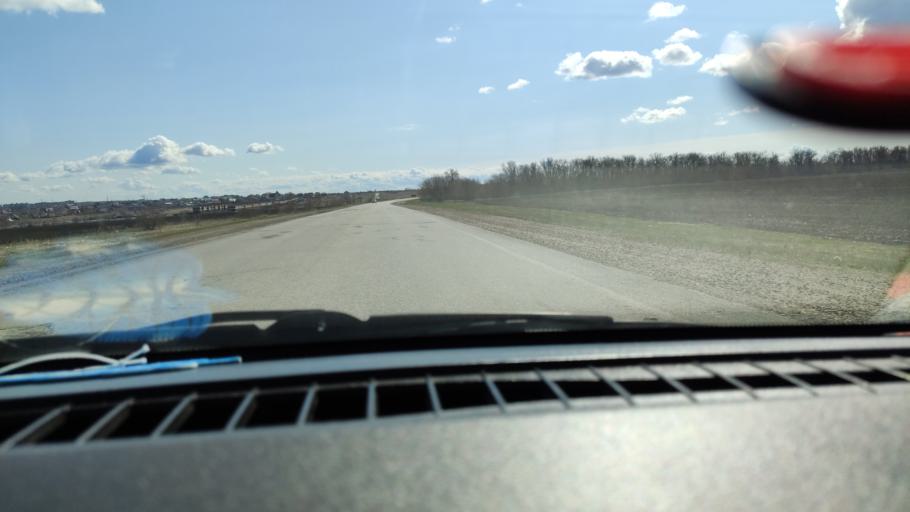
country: RU
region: Samara
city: Varlamovo
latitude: 53.1159
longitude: 48.3464
